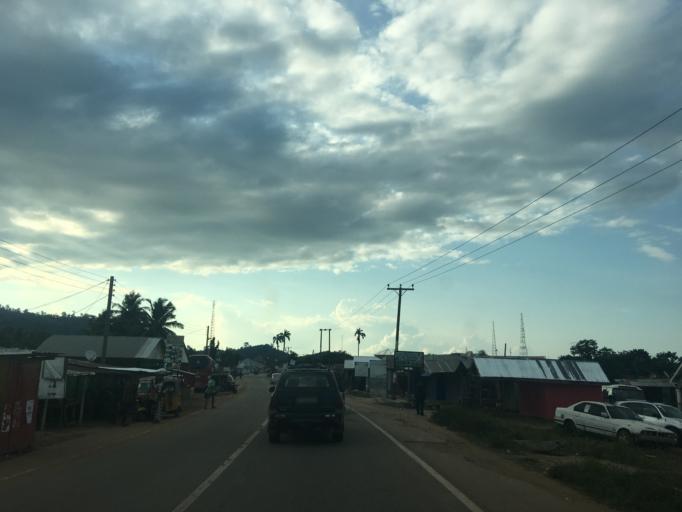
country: GH
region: Western
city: Bibiani
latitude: 6.4492
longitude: -2.3155
